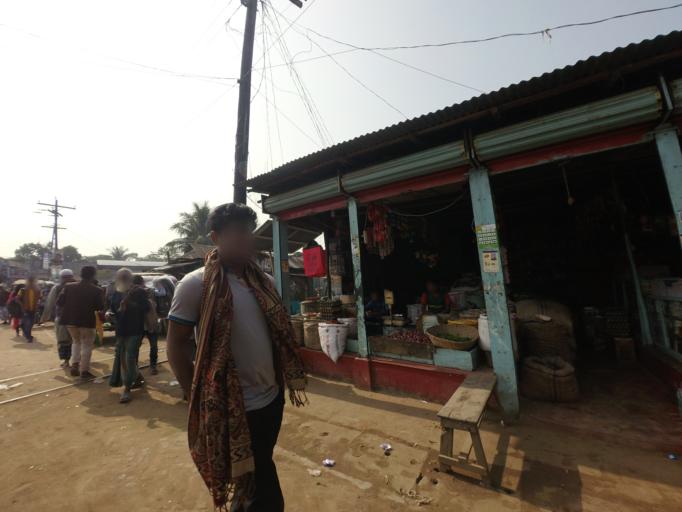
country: BD
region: Dhaka
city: Netrakona
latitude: 25.0102
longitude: 90.6488
